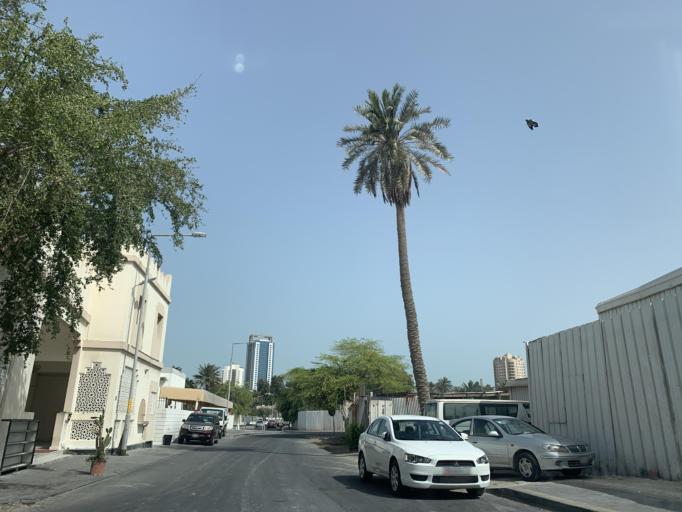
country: BH
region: Manama
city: Manama
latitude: 26.2237
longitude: 50.5684
